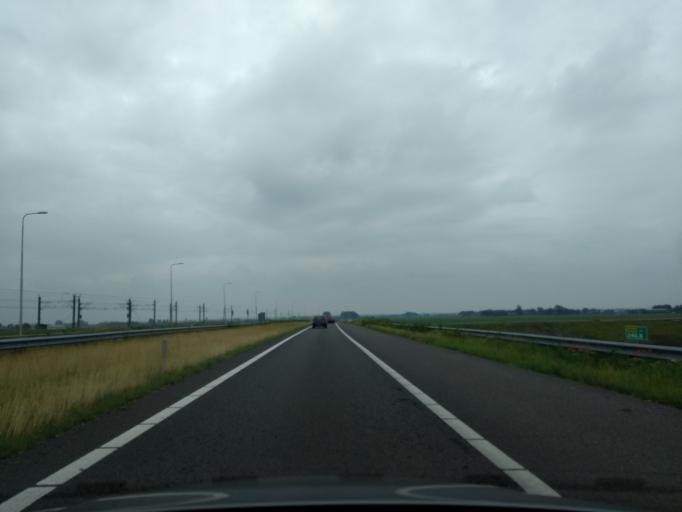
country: NL
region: Overijssel
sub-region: Gemeente Kampen
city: Kampen
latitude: 52.5242
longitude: 5.9226
